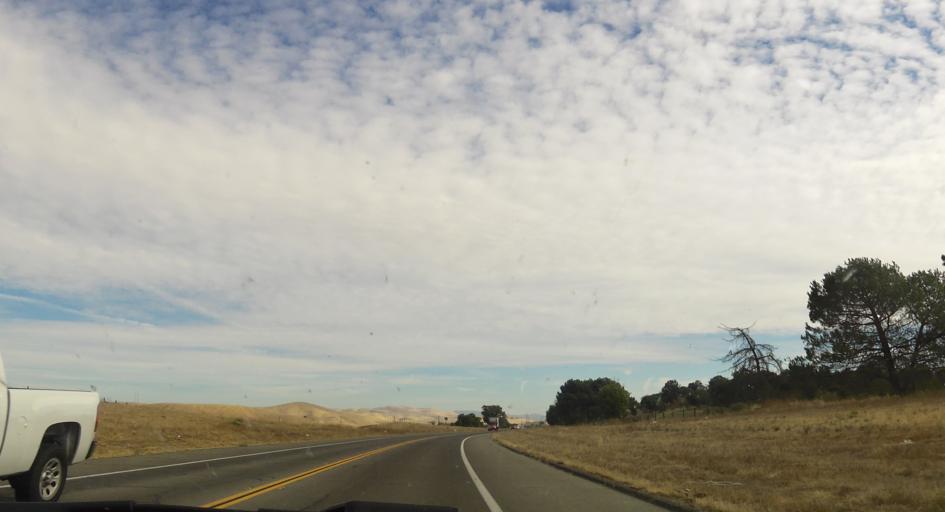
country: US
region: California
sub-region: San Benito County
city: Ridgemark
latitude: 36.8130
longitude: -121.3503
